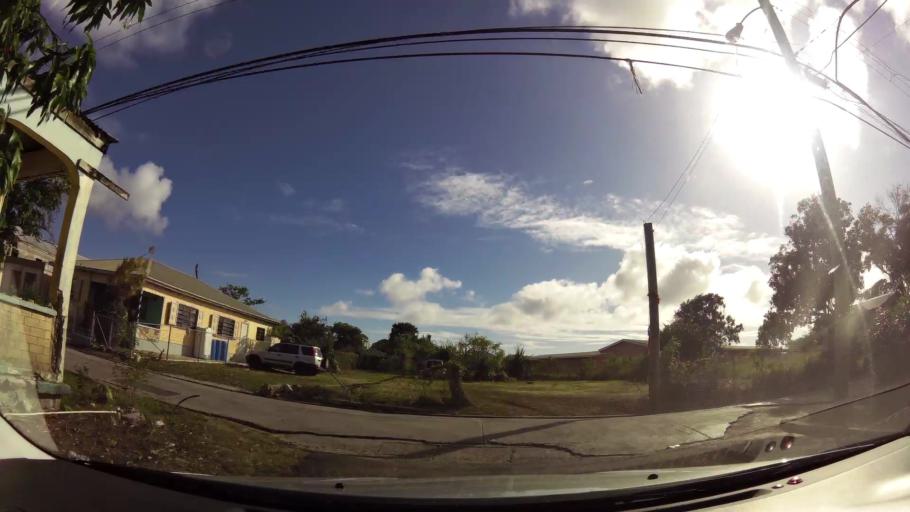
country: AG
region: Saint Peter
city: All Saints
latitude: 17.0641
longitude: -61.7931
